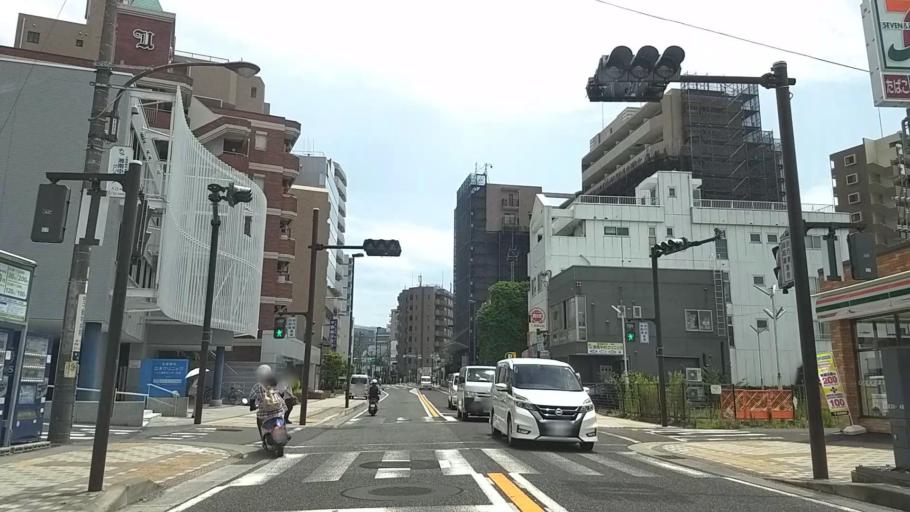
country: JP
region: Kanagawa
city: Fujisawa
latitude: 35.3434
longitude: 139.4879
